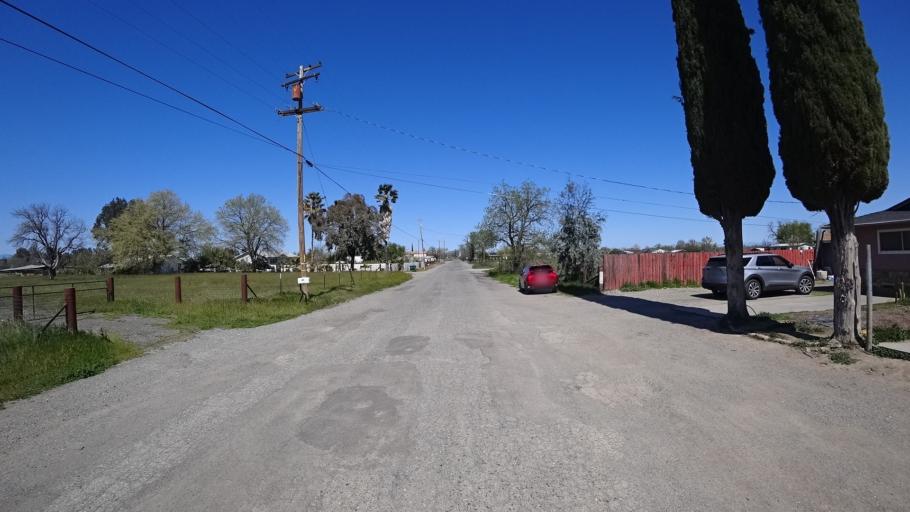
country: US
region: California
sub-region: Glenn County
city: Orland
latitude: 39.7791
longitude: -122.2477
